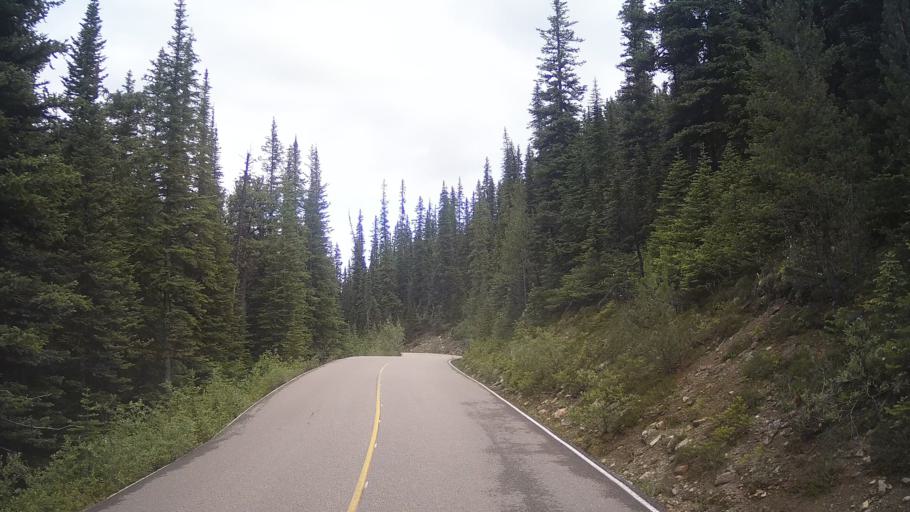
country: CA
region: Alberta
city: Jasper Park Lodge
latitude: 52.6950
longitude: -118.0581
